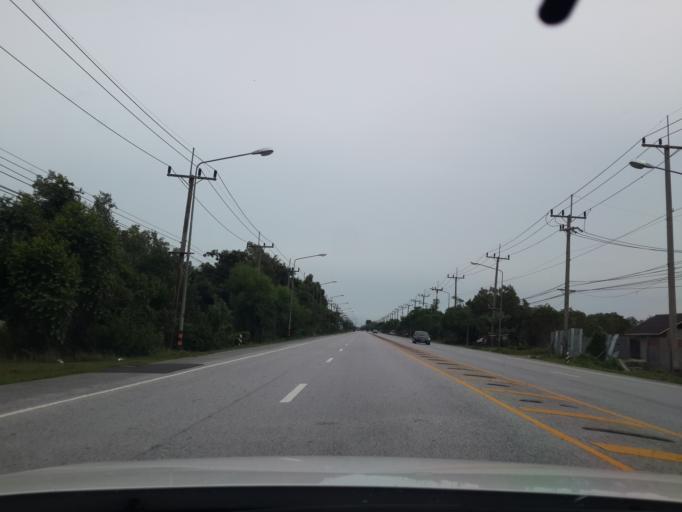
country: TH
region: Pattani
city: Nong Chik
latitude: 6.8086
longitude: 101.1548
